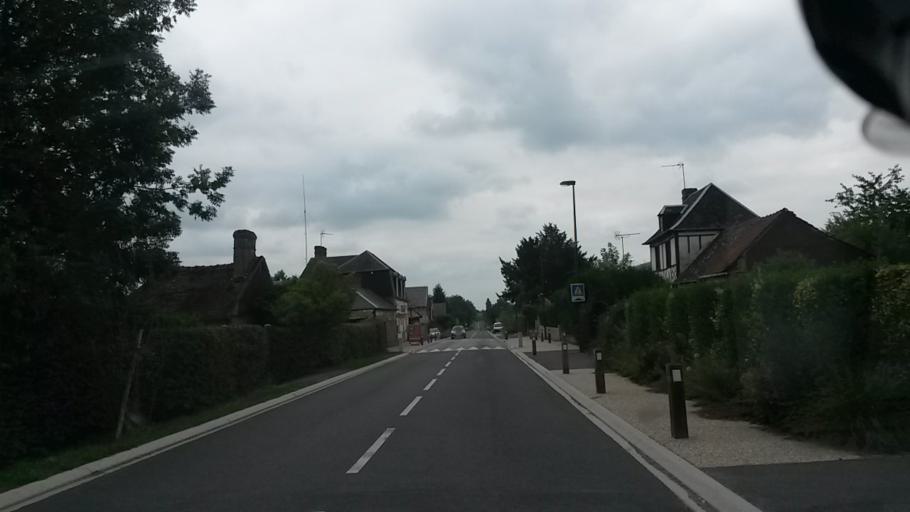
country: FR
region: Haute-Normandie
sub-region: Departement de la Seine-Maritime
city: Forges-les-Eaux
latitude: 49.5708
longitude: 1.5353
